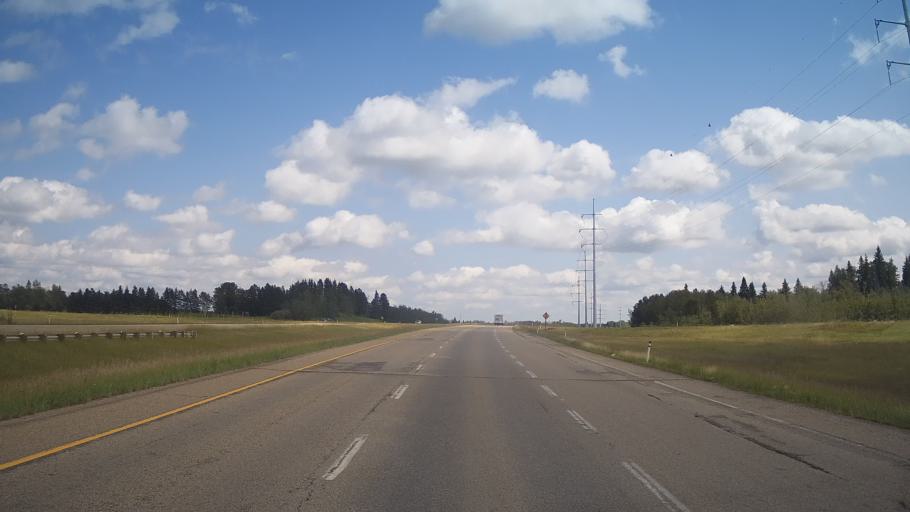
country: CA
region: Alberta
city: Sherwood Park
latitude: 53.4466
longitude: -113.2455
